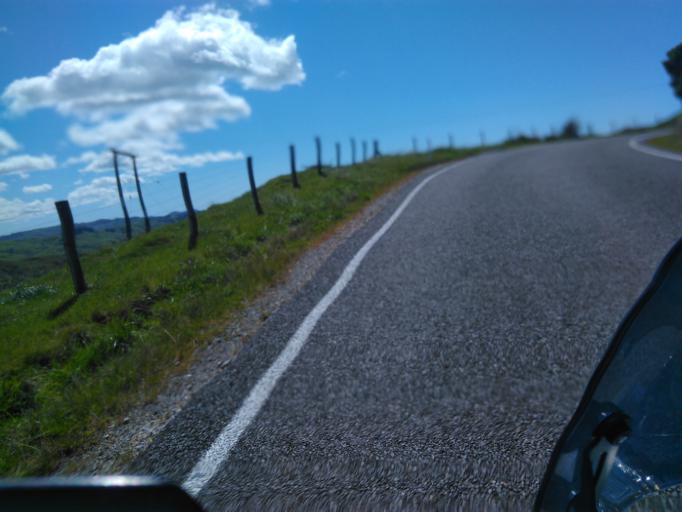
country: NZ
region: Gisborne
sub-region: Gisborne District
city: Gisborne
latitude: -38.5310
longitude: 178.2137
